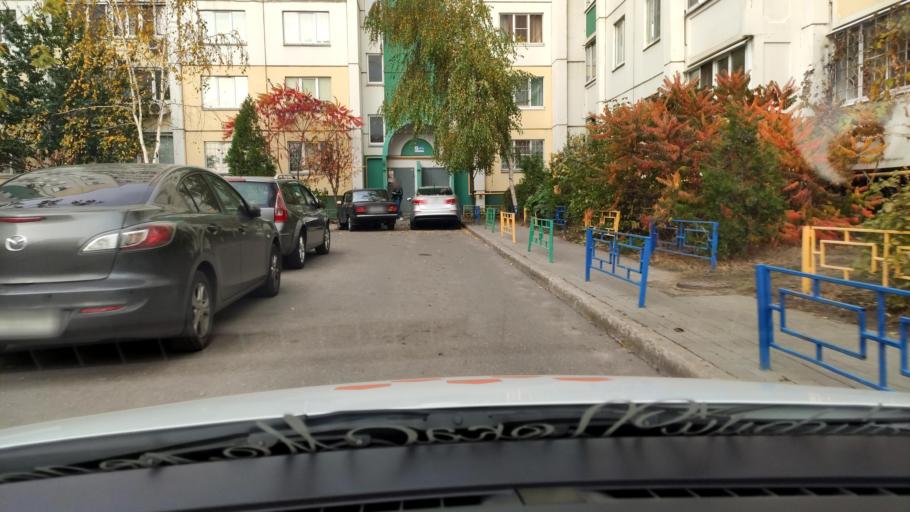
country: RU
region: Voronezj
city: Pridonskoy
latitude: 51.6796
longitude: 39.1238
